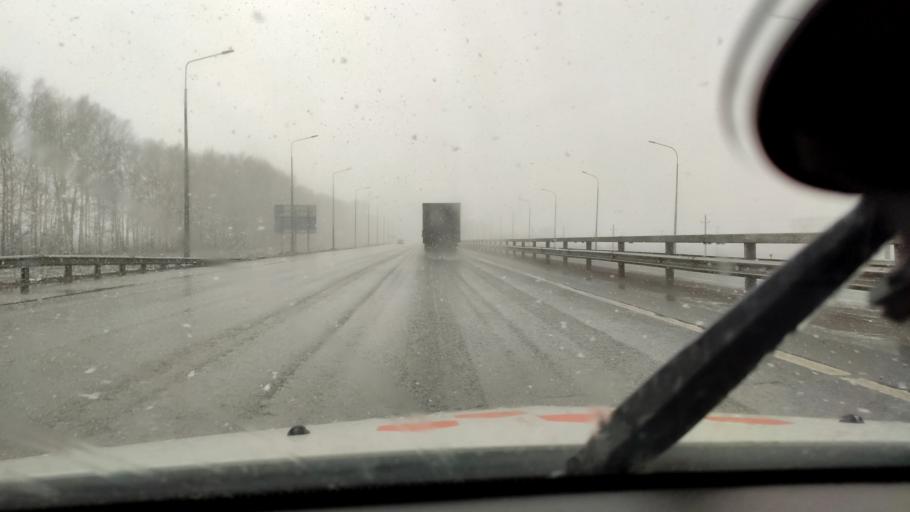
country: RU
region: Bashkortostan
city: Buzdyak
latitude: 54.6488
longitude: 54.5922
